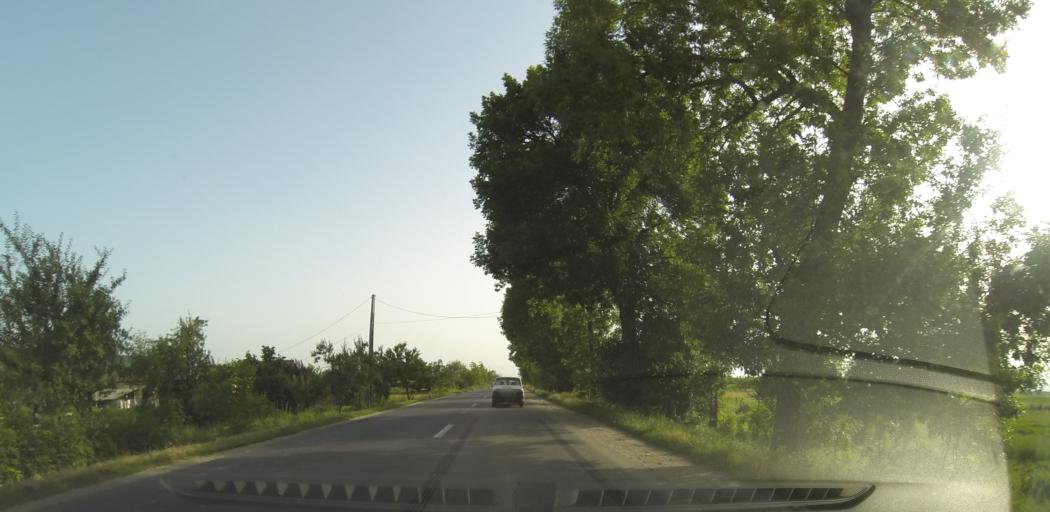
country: RO
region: Valcea
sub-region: Comuna Babeni
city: Valea Mare
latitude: 44.8947
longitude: 24.2320
